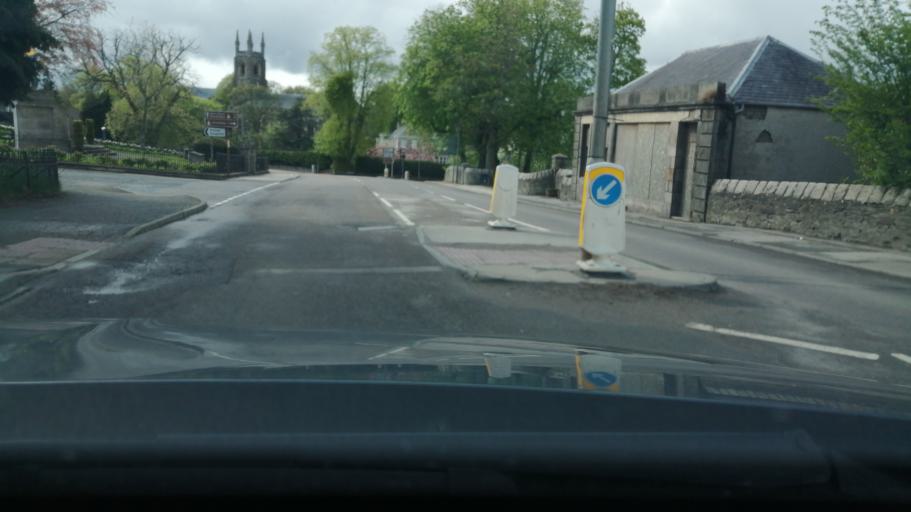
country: GB
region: Scotland
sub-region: Moray
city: Keith
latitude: 57.5433
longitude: -2.9508
